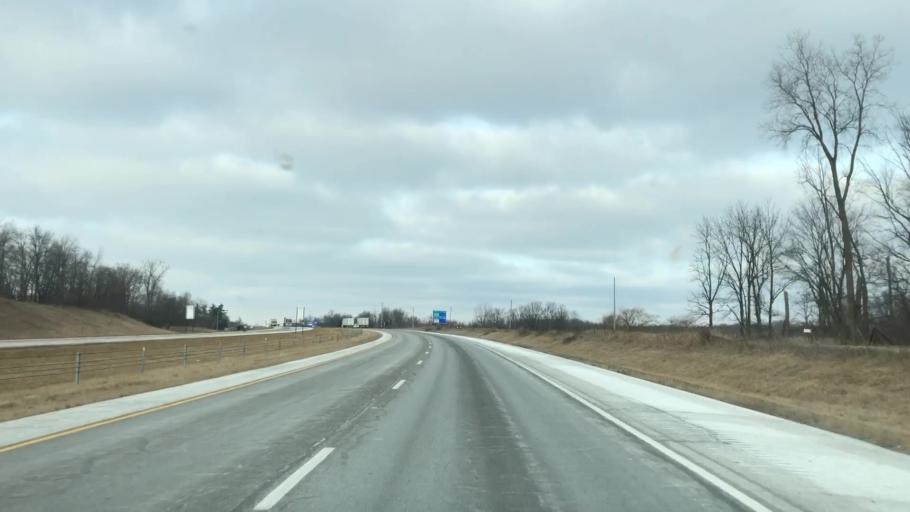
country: US
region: Indiana
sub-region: Steuben County
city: Angola
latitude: 41.6037
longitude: -85.0461
